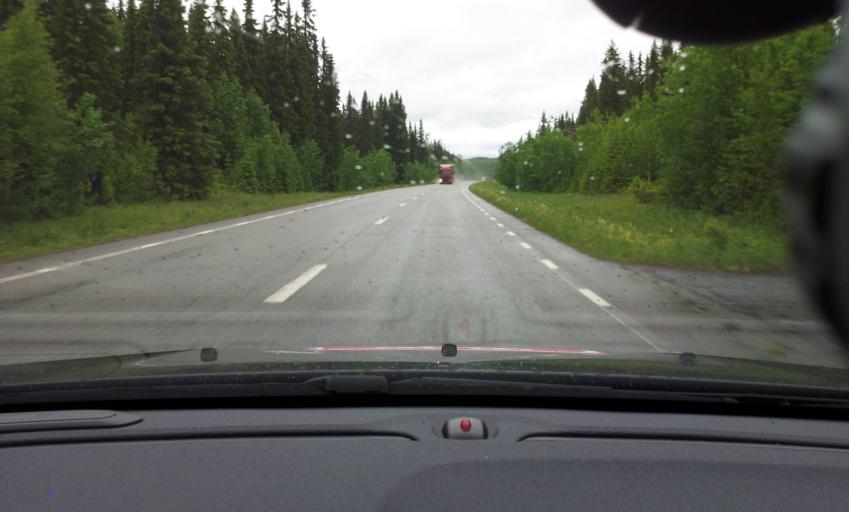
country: SE
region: Jaemtland
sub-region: Krokoms Kommun
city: Krokom
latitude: 63.5333
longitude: 14.5668
